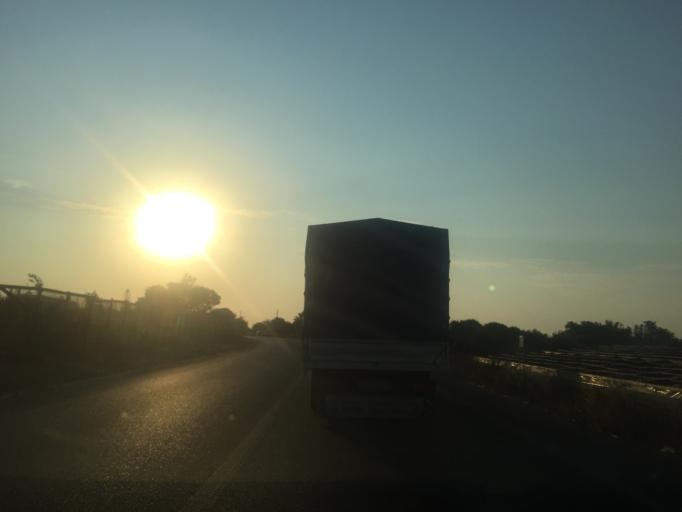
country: IT
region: Sicily
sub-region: Ragusa
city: Cava d'Aliga
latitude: 36.7195
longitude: 14.7066
